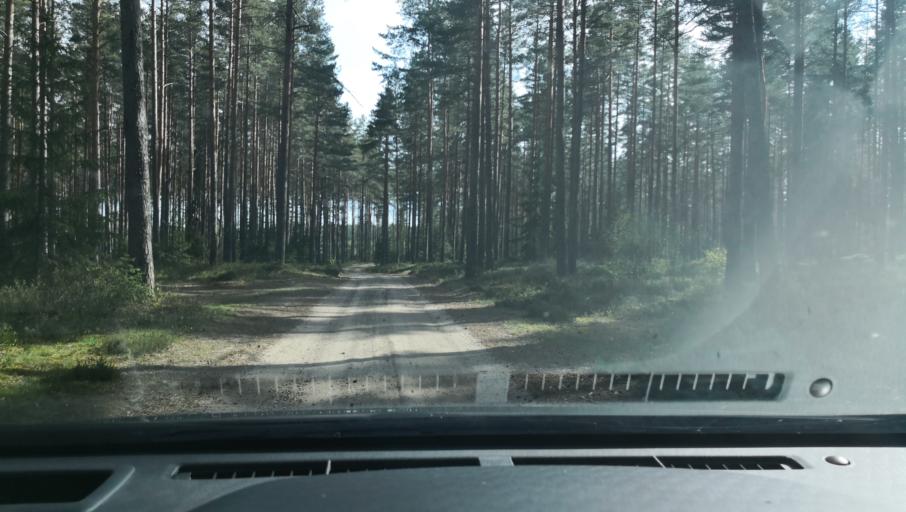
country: SE
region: OErebro
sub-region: Askersunds Kommun
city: Asbro
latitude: 59.0269
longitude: 15.0546
